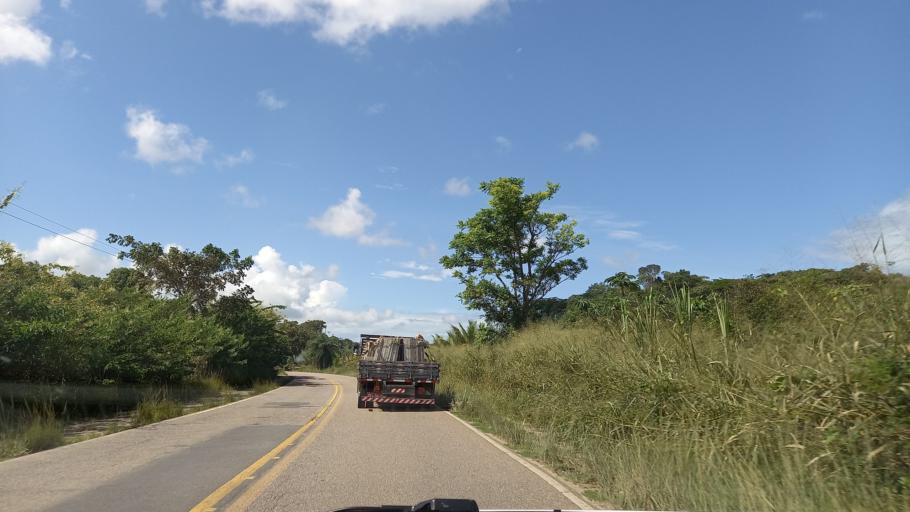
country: BR
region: Pernambuco
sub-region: Barreiros
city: Barreiros
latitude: -8.7814
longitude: -35.1760
